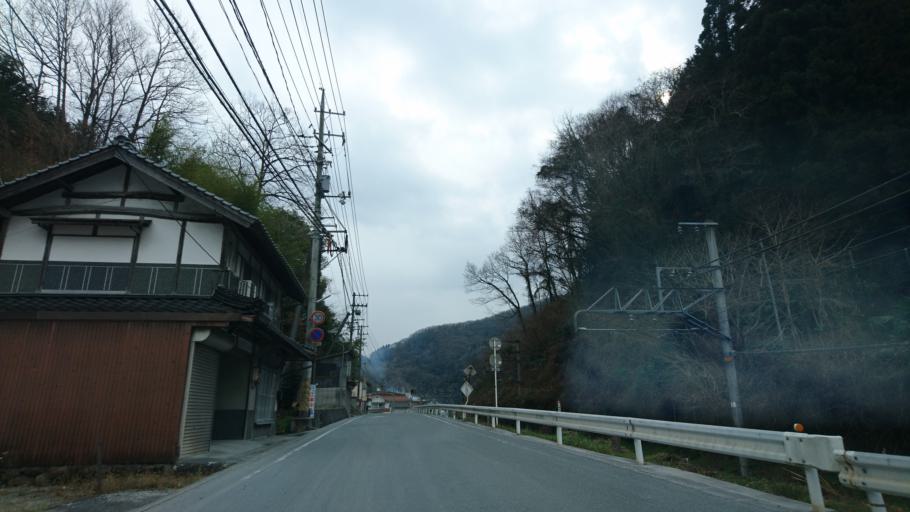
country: JP
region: Okayama
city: Niimi
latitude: 34.9288
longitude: 133.5206
